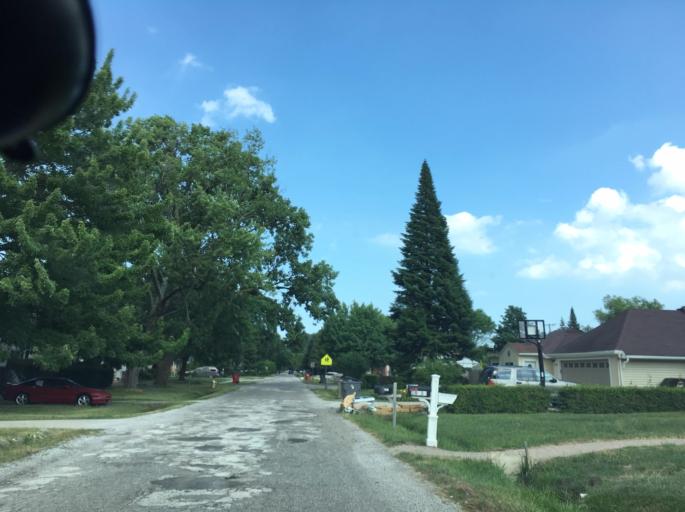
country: US
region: Michigan
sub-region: Macomb County
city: Fraser
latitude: 42.5460
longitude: -82.9143
